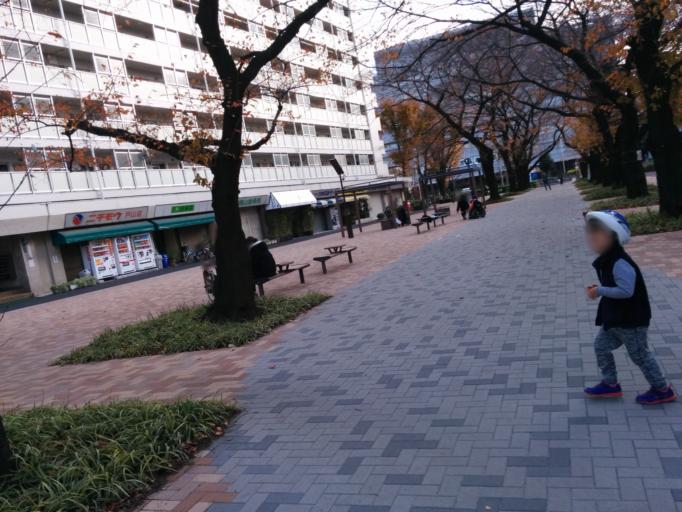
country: JP
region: Tokyo
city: Tokyo
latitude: 35.7022
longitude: 139.7146
